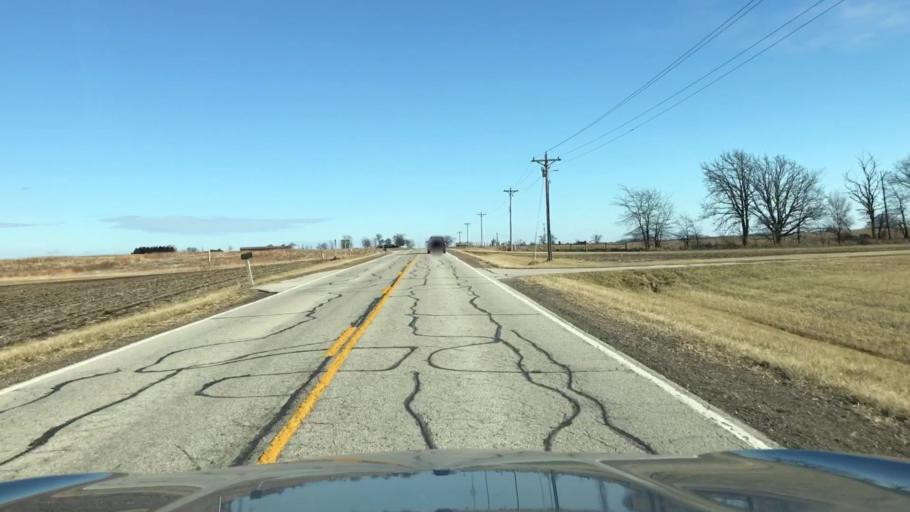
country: US
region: Illinois
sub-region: McLean County
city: Lexington
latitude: 40.6451
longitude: -88.8288
